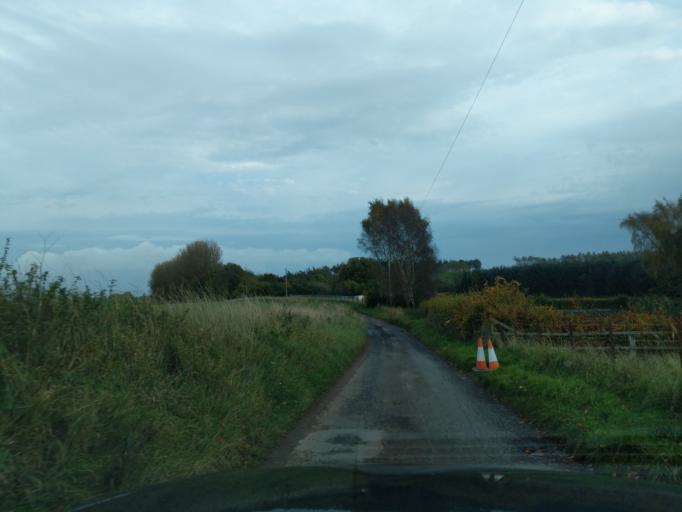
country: GB
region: Scotland
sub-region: Fife
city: Tayport
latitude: 56.4238
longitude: -2.9045
